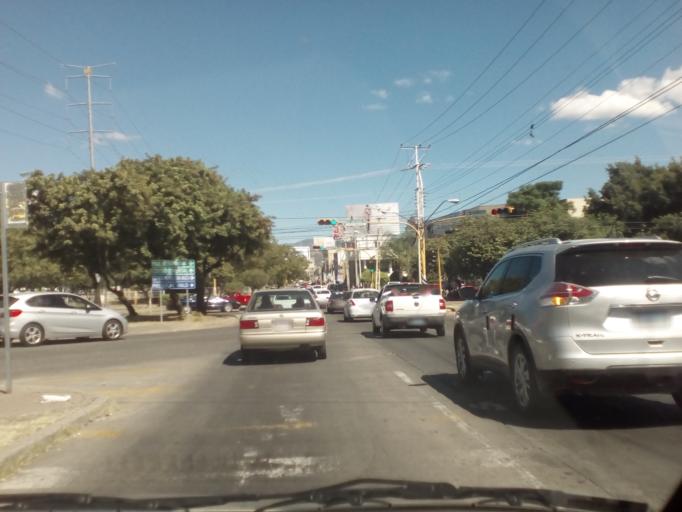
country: MX
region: Guanajuato
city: Leon
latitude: 21.1540
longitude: -101.6971
